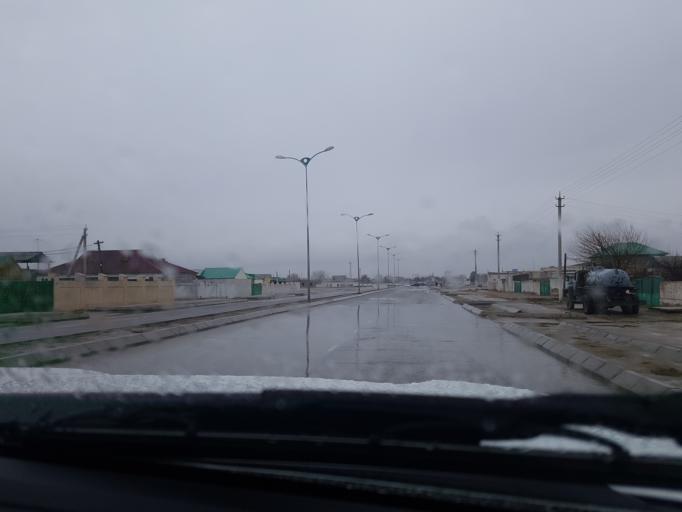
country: TM
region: Balkan
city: Balkanabat
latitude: 39.6322
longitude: 54.2395
